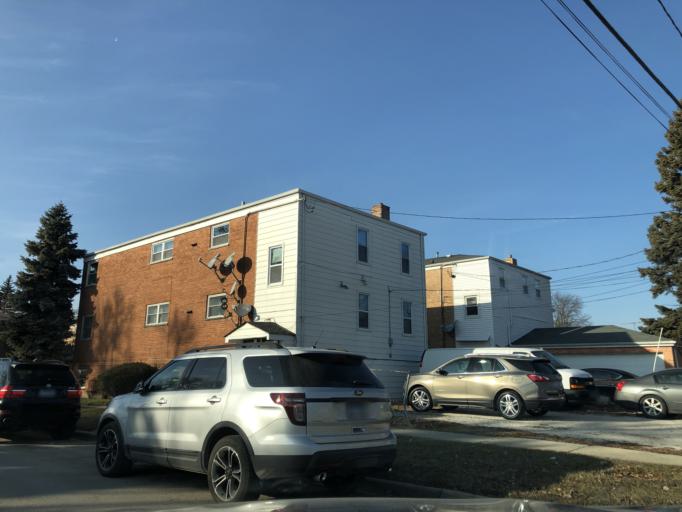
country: US
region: Illinois
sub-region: Cook County
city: Maywood
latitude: 41.8773
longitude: -87.8322
